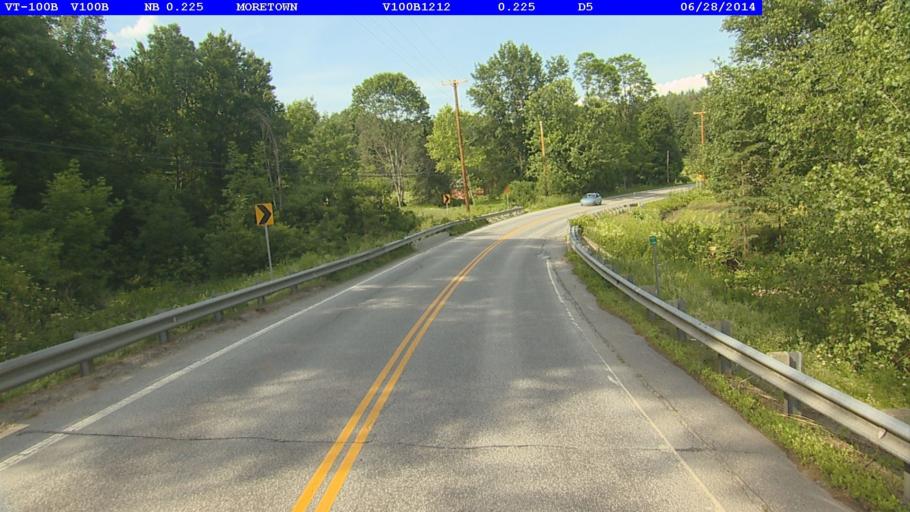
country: US
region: Vermont
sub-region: Washington County
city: Waterbury
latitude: 44.2436
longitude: -72.7749
